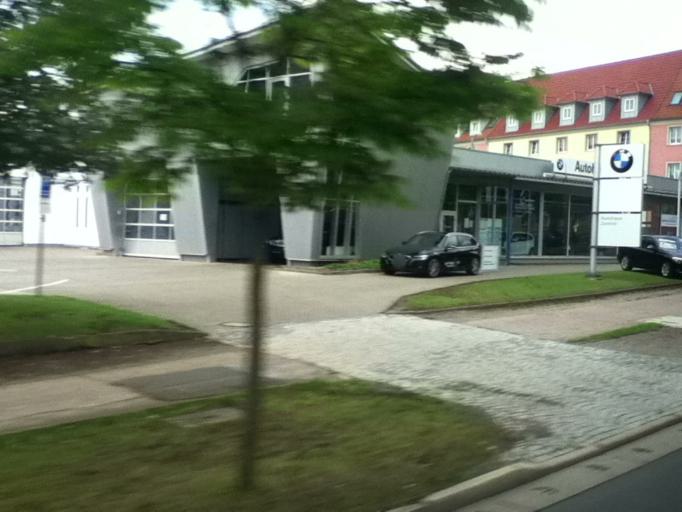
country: DE
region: Thuringia
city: Weimar
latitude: 50.9949
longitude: 11.3194
